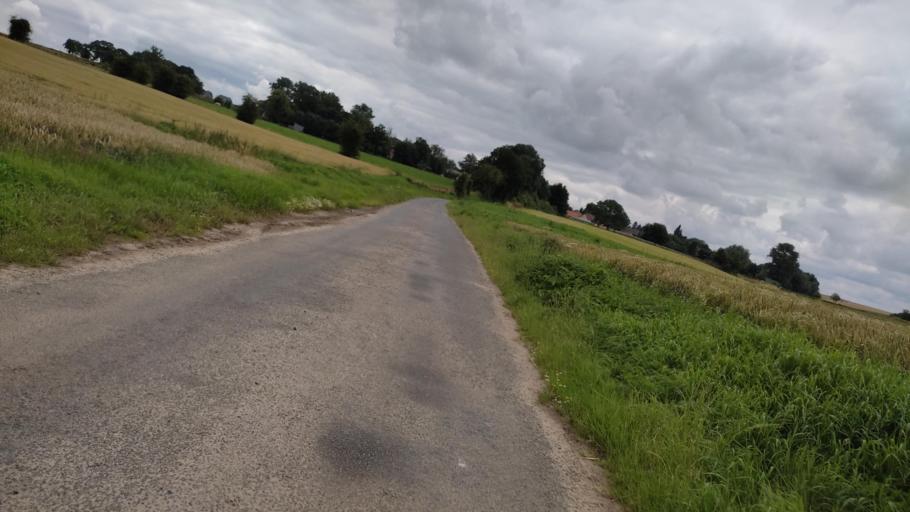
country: FR
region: Nord-Pas-de-Calais
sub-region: Departement du Pas-de-Calais
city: Beaumetz-les-Loges
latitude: 50.2452
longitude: 2.6325
